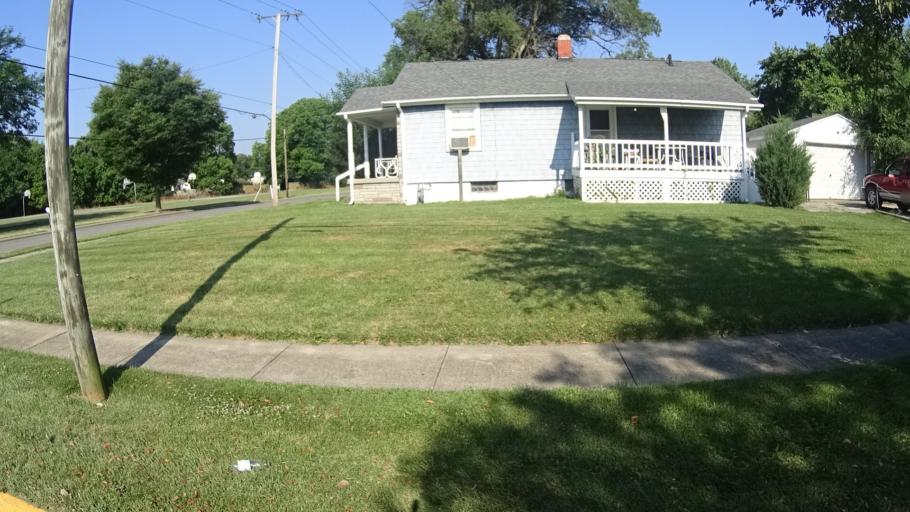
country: US
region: Ohio
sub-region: Erie County
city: Sandusky
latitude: 41.4475
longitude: -82.6810
